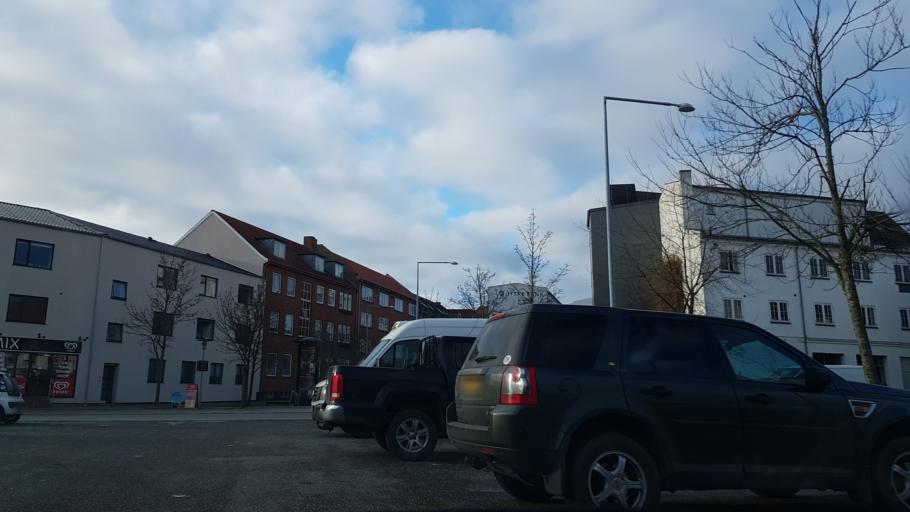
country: DK
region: Zealand
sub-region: Slagelse Kommune
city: Slagelse
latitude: 55.4023
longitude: 11.3564
